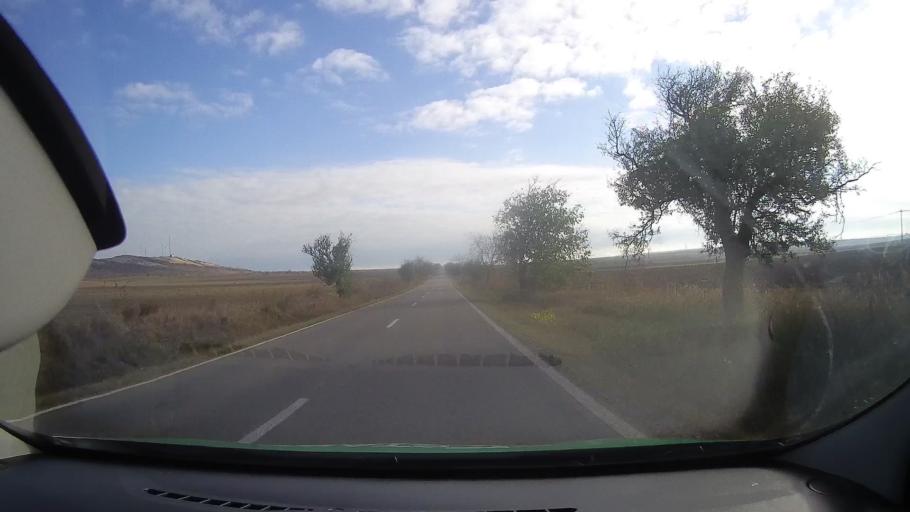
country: RO
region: Tulcea
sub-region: Comuna Mahmudia
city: Mahmudia
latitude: 45.0779
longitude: 29.0495
